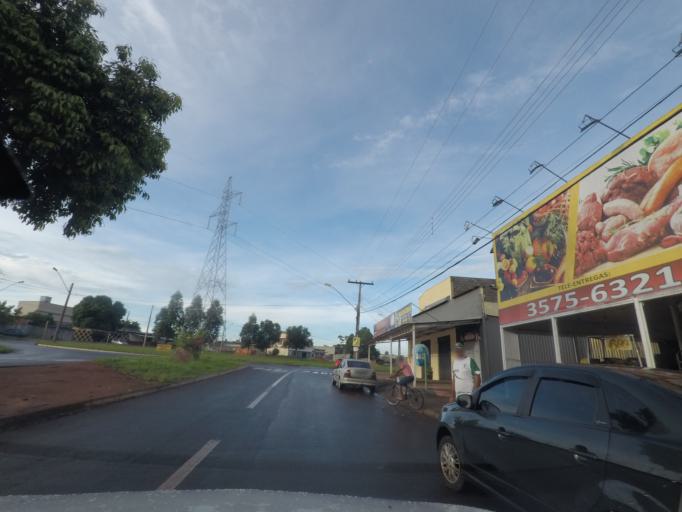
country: BR
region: Goias
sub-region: Goiania
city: Goiania
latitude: -16.7380
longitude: -49.3690
